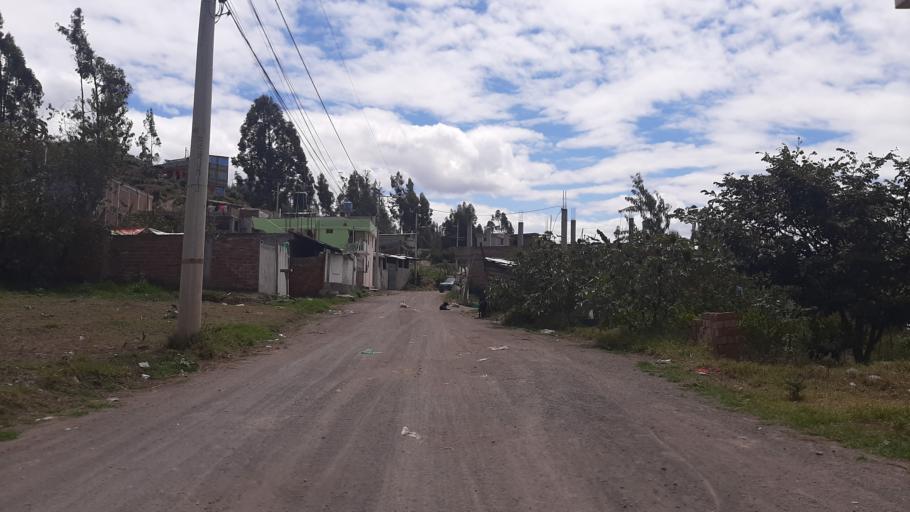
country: EC
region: Chimborazo
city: Riobamba
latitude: -1.6505
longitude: -78.6370
